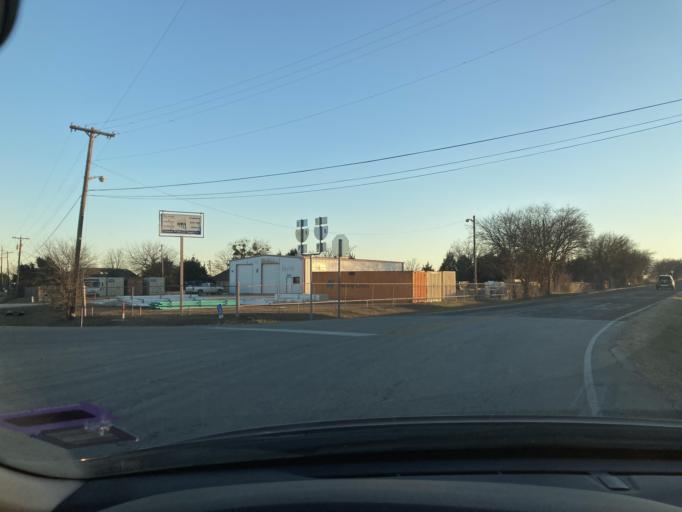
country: US
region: Texas
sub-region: Ellis County
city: Waxahachie
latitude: 32.3702
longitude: -96.8610
